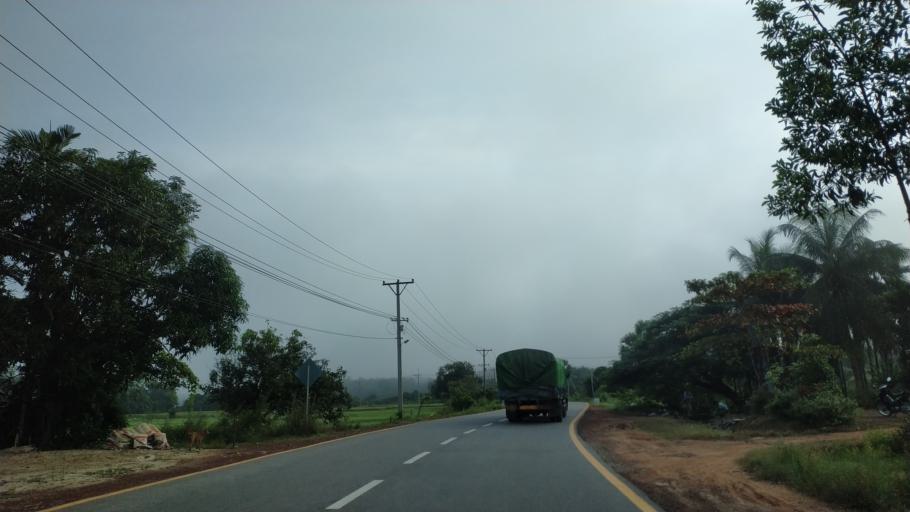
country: MM
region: Tanintharyi
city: Dawei
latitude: 14.2023
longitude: 98.2045
